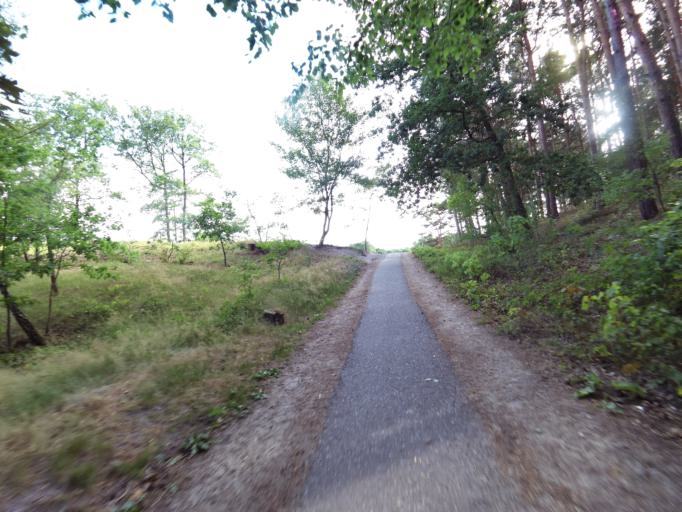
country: NL
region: Limburg
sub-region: Gemeente Brunssum
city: Brunssum
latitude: 50.9289
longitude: 5.9869
